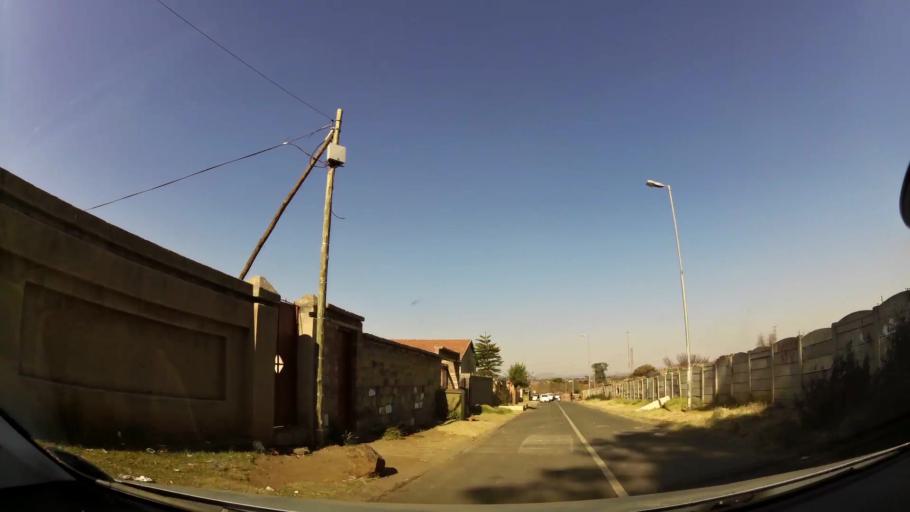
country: ZA
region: Gauteng
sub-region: City of Johannesburg Metropolitan Municipality
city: Soweto
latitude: -26.2788
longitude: 27.8748
